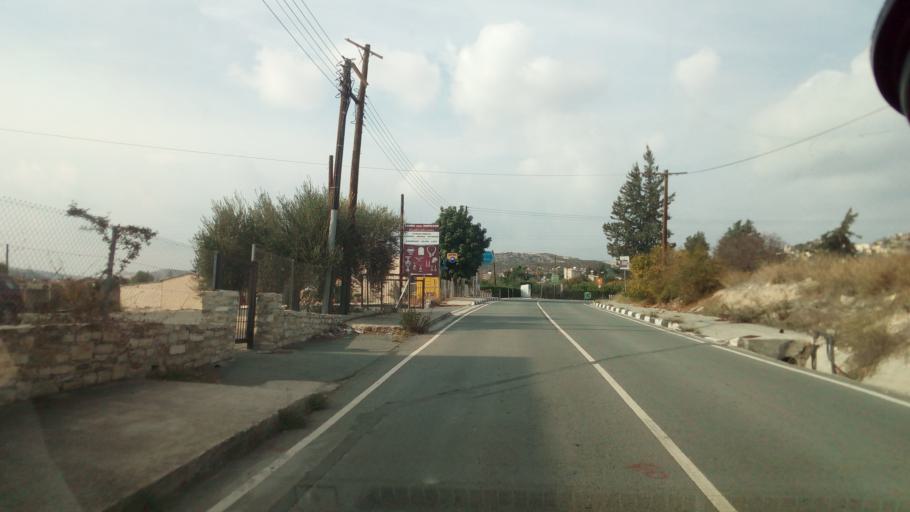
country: CY
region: Larnaka
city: Kofinou
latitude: 34.8171
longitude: 33.3601
